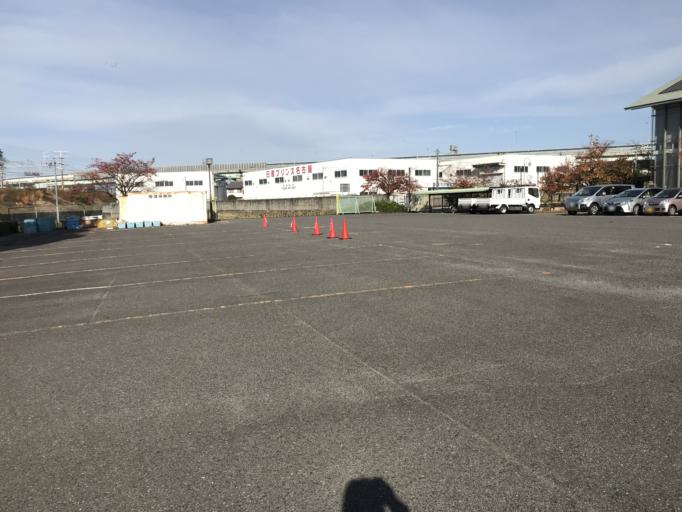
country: JP
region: Aichi
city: Inazawa
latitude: 35.2180
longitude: 136.8418
